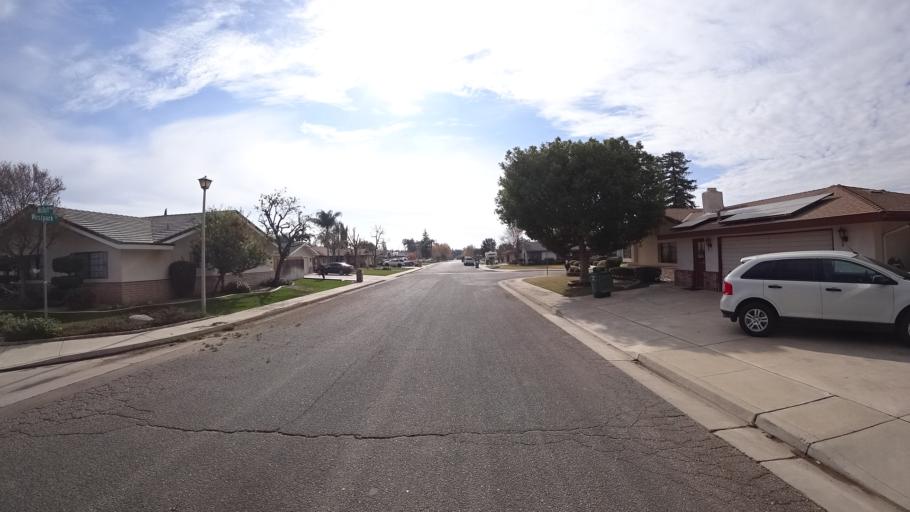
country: US
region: California
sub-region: Kern County
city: Greenacres
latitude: 35.4079
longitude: -119.0878
